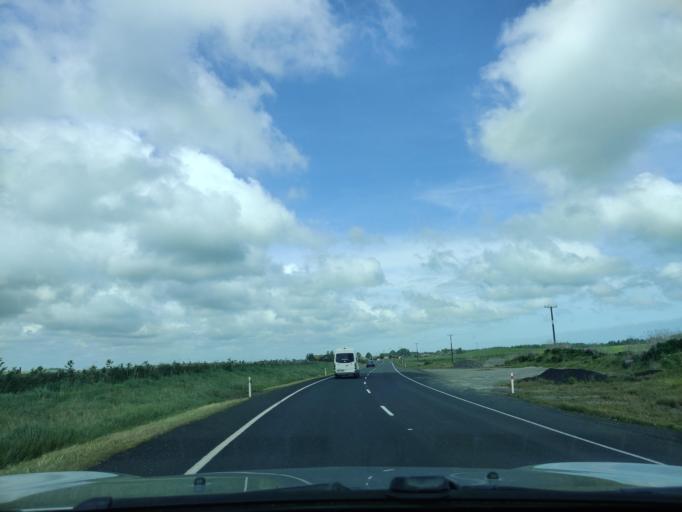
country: NZ
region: Manawatu-Wanganui
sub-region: Wanganui District
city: Wanganui
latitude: -39.8143
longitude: 174.8242
